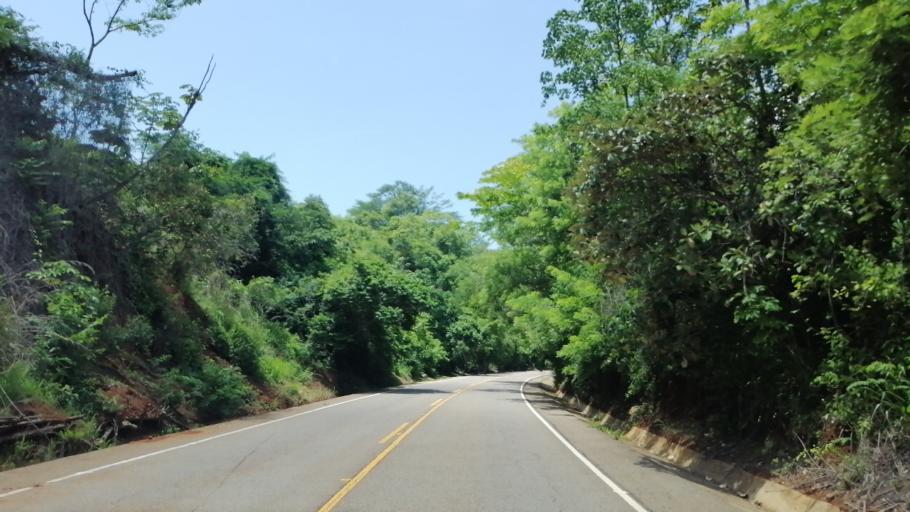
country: SV
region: Chalatenango
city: Nueva Concepcion
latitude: 14.1772
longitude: -89.3178
